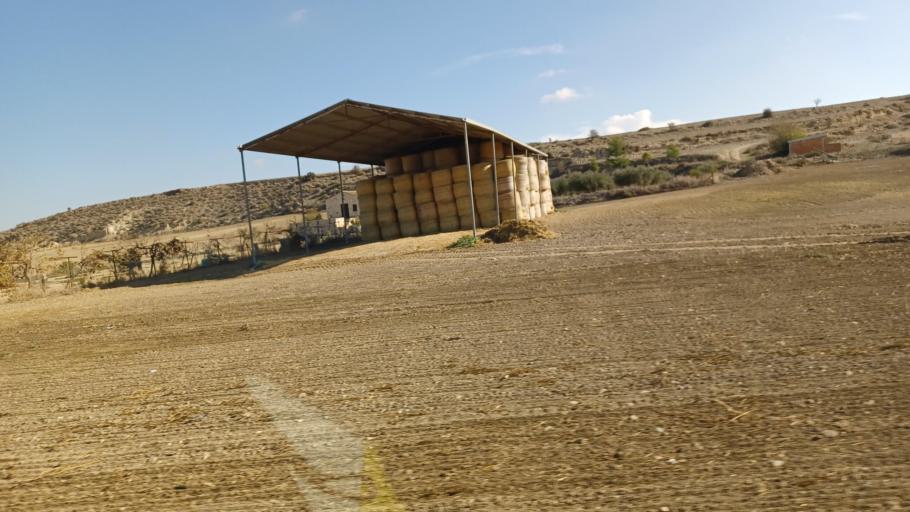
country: CY
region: Larnaka
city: Athienou
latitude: 35.0415
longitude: 33.5561
